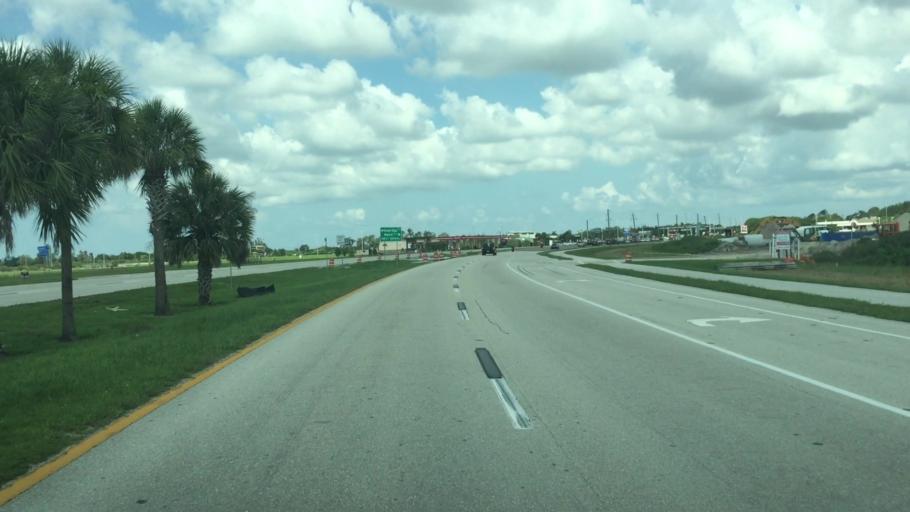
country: US
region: Florida
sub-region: Lee County
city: Villas
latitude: 26.5285
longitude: -81.8475
